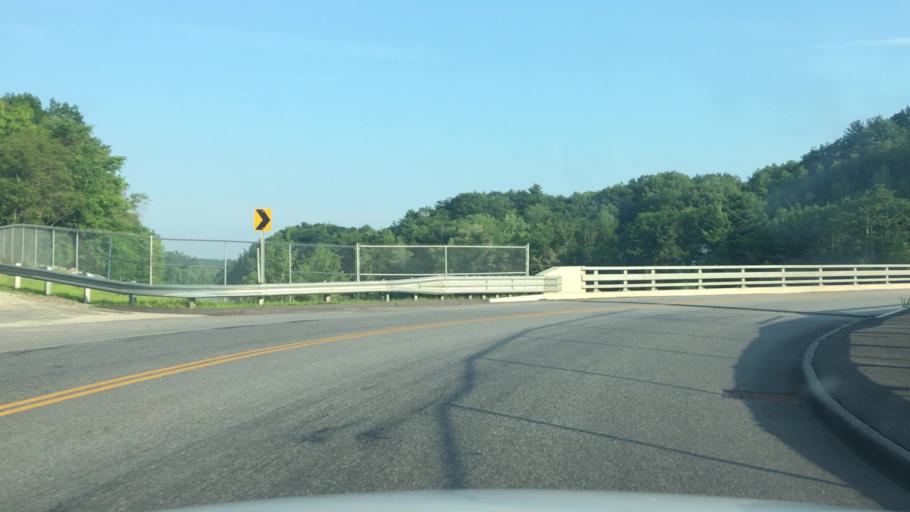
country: US
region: Maine
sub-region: Androscoggin County
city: Lisbon Falls
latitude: 43.9937
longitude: -70.0583
